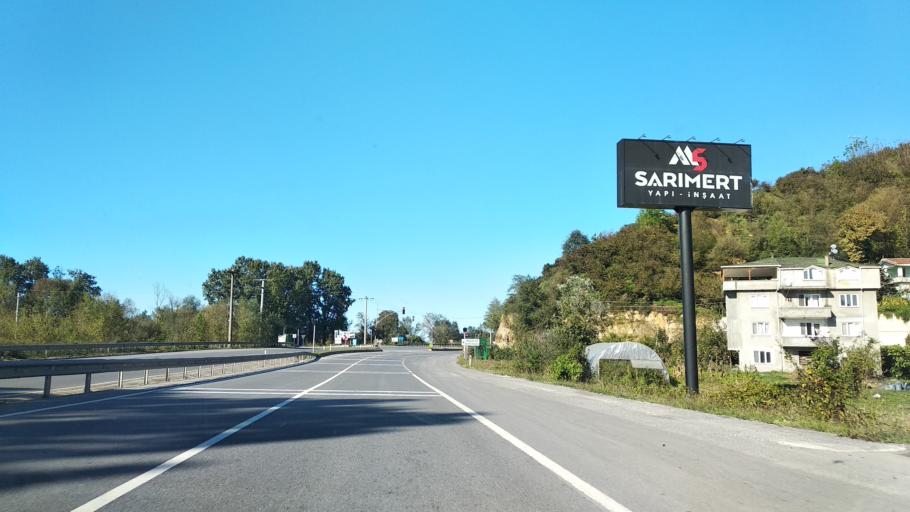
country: TR
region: Sakarya
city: Karasu
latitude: 41.0795
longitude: 30.6459
